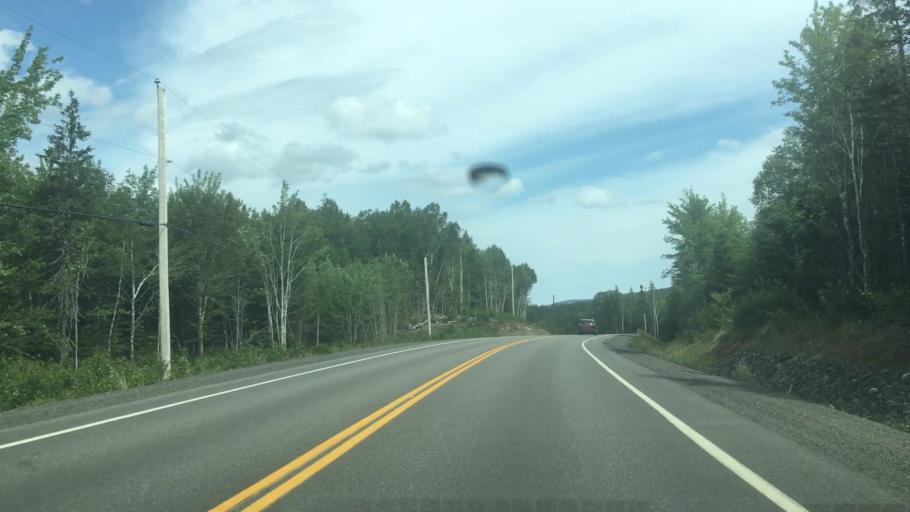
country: CA
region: Nova Scotia
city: Sydney Mines
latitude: 46.3141
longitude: -60.6124
